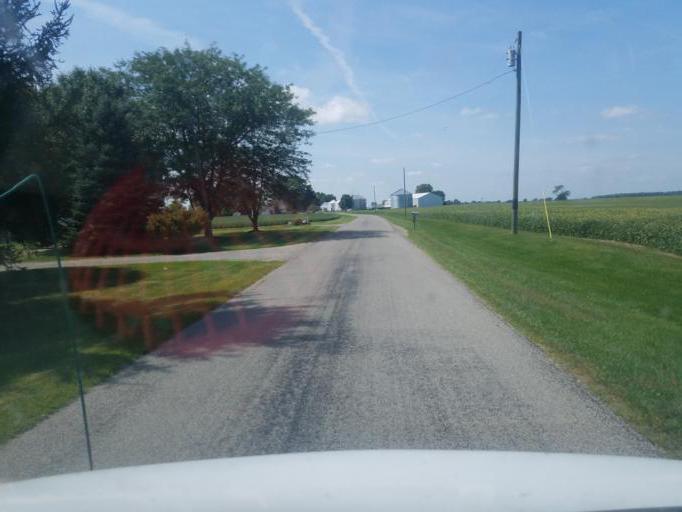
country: US
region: Ohio
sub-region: Union County
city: Richwood
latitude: 40.3562
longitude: -83.2684
